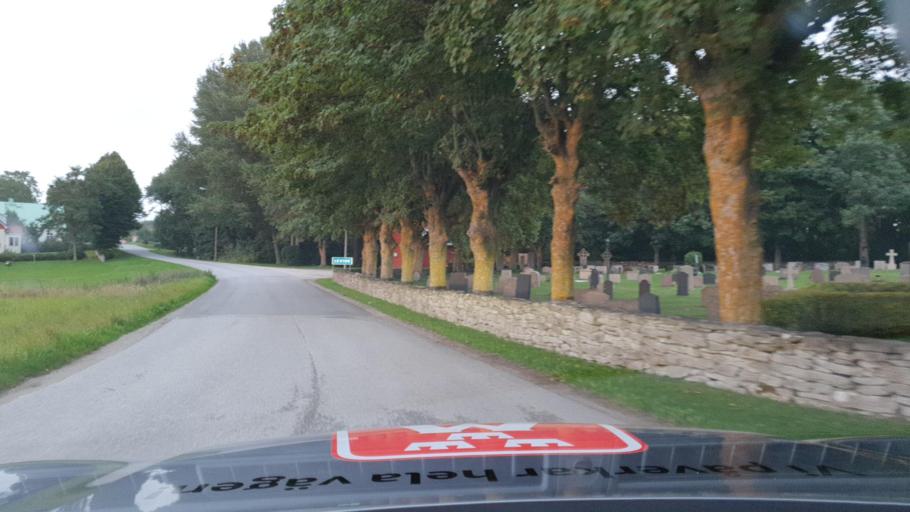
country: SE
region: Gotland
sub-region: Gotland
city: Hemse
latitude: 57.2824
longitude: 18.2660
